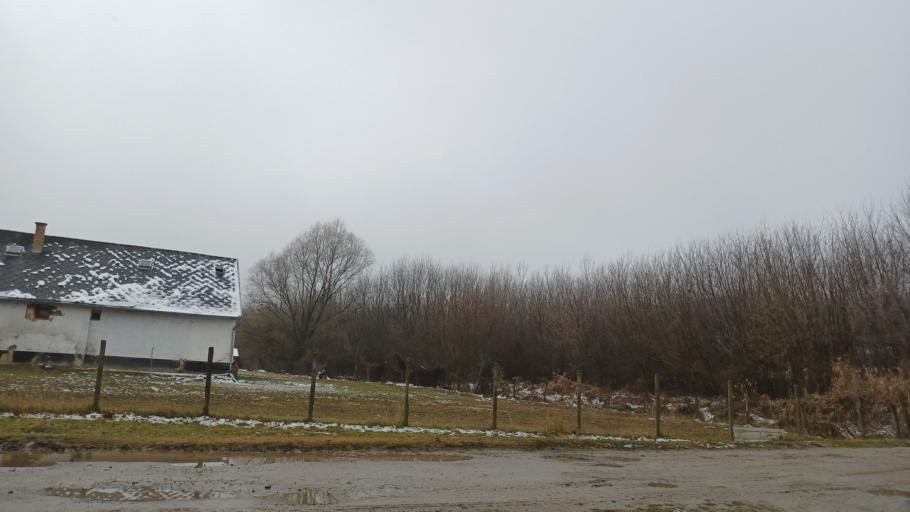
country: HU
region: Tolna
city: Pincehely
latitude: 46.6348
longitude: 18.4896
